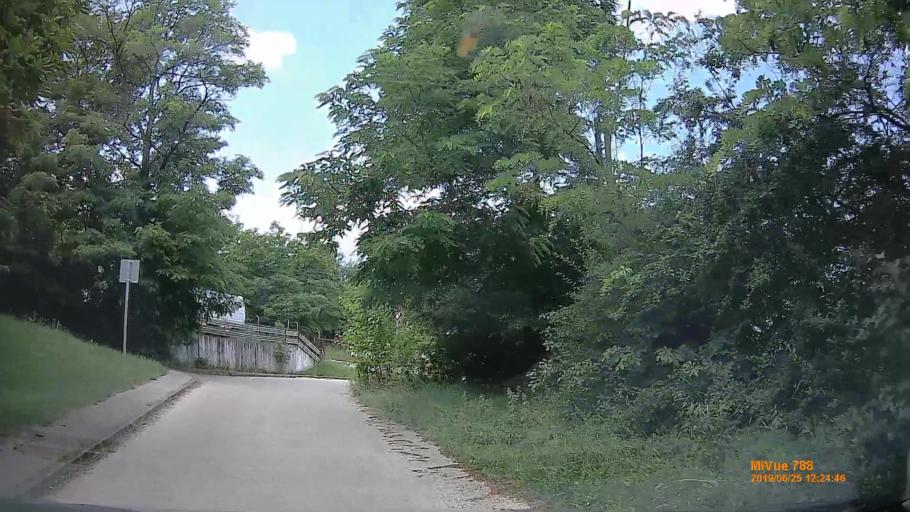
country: HU
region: Komarom-Esztergom
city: Dorog
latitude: 47.7196
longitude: 18.7234
